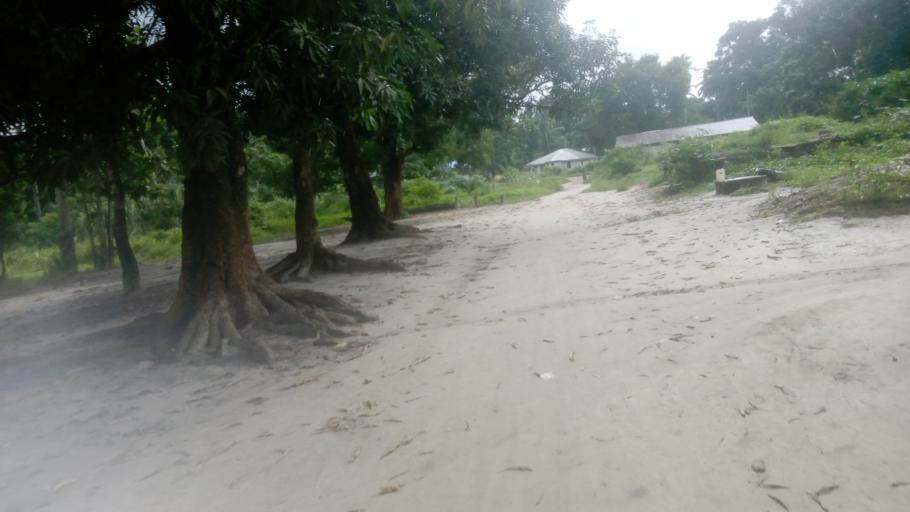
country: SL
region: Northern Province
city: Lunsar
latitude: 8.6847
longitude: -12.5401
